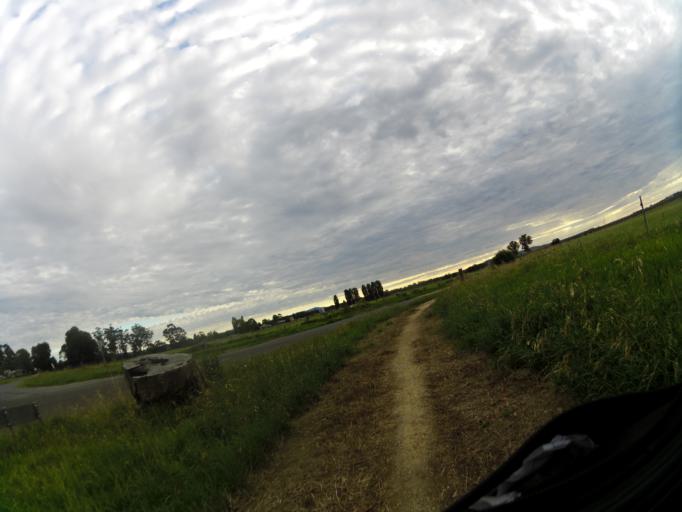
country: AU
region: Victoria
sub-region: East Gippsland
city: Lakes Entrance
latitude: -37.7242
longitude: 148.4414
